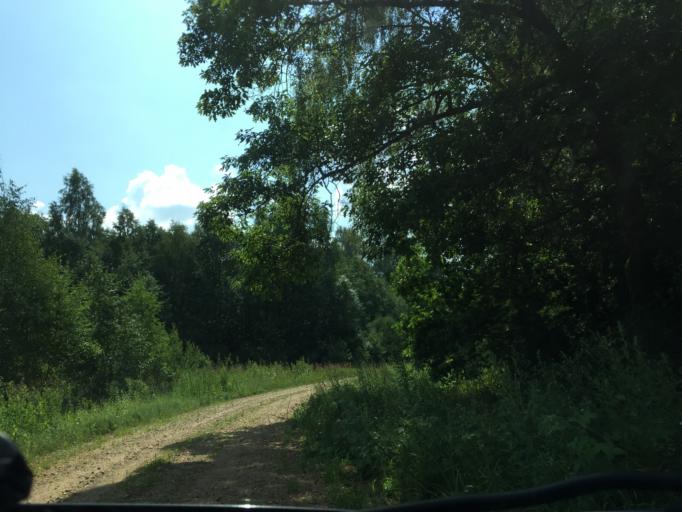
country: LT
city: Zagare
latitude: 56.3848
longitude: 23.2055
